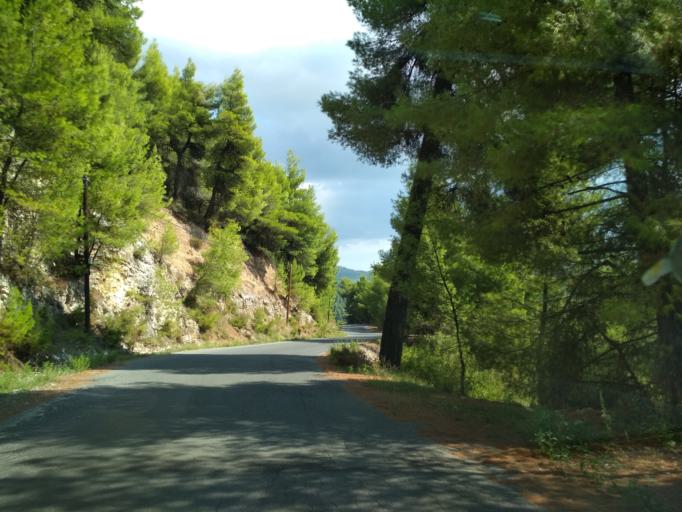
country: GR
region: Central Greece
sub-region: Nomos Evvoias
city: Roviai
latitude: 38.8243
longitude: 23.2785
